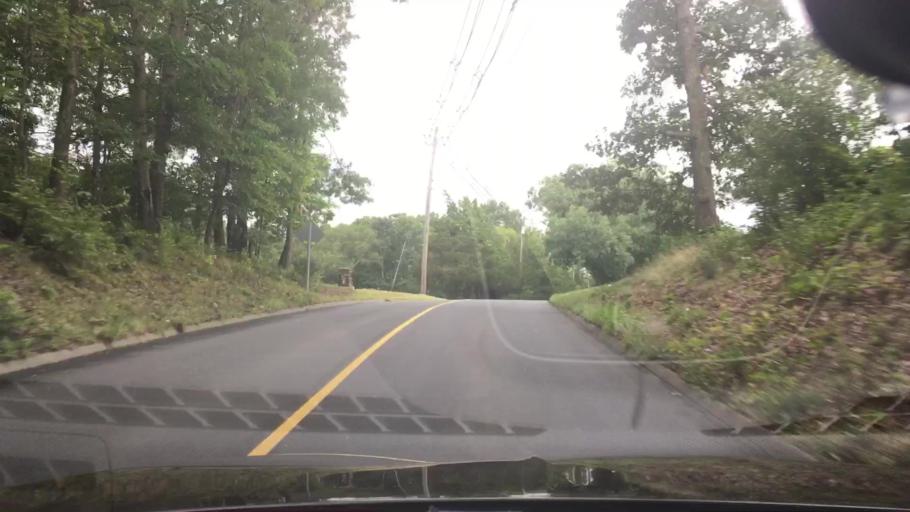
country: US
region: Connecticut
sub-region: New Haven County
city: Madison
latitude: 41.3304
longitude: -72.5884
